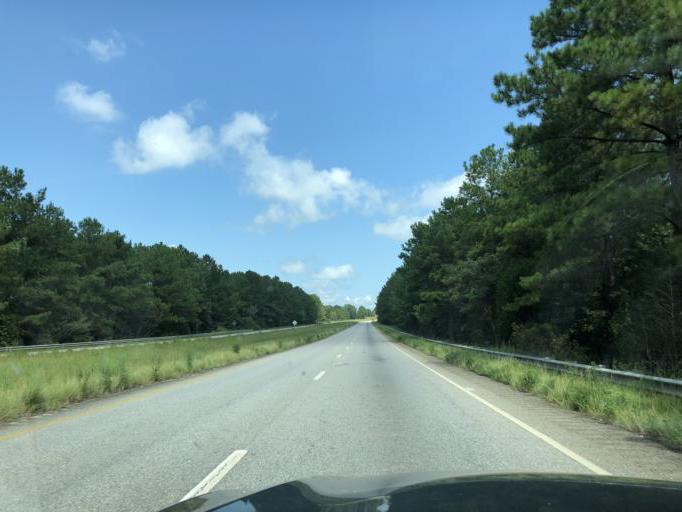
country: US
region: Alabama
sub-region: Henry County
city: Abbeville
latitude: 31.6914
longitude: -85.2787
